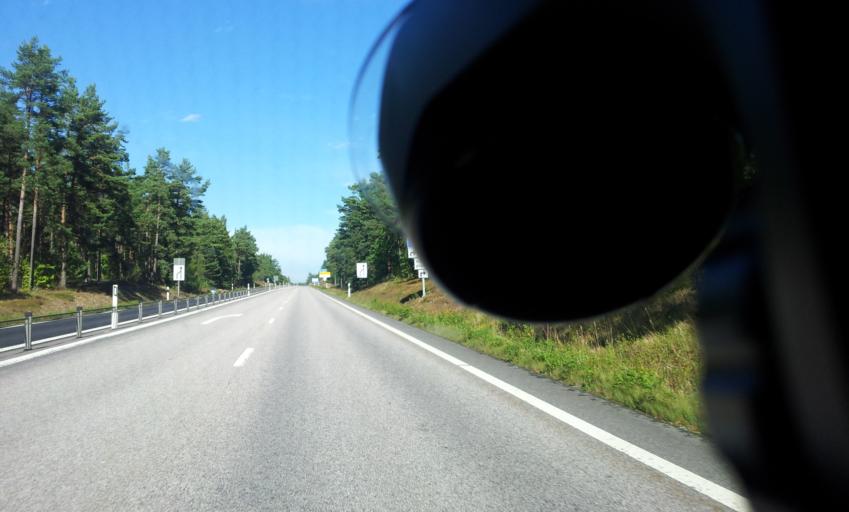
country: SE
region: Kalmar
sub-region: Oskarshamns Kommun
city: Oskarshamn
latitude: 57.3475
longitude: 16.4898
